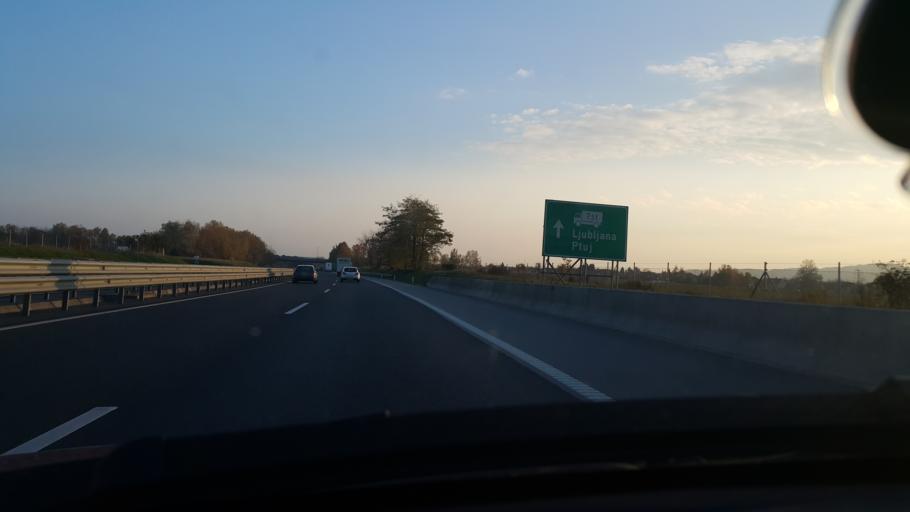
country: SI
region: Hoce-Slivnica
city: Rogoza
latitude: 46.5047
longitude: 15.6686
